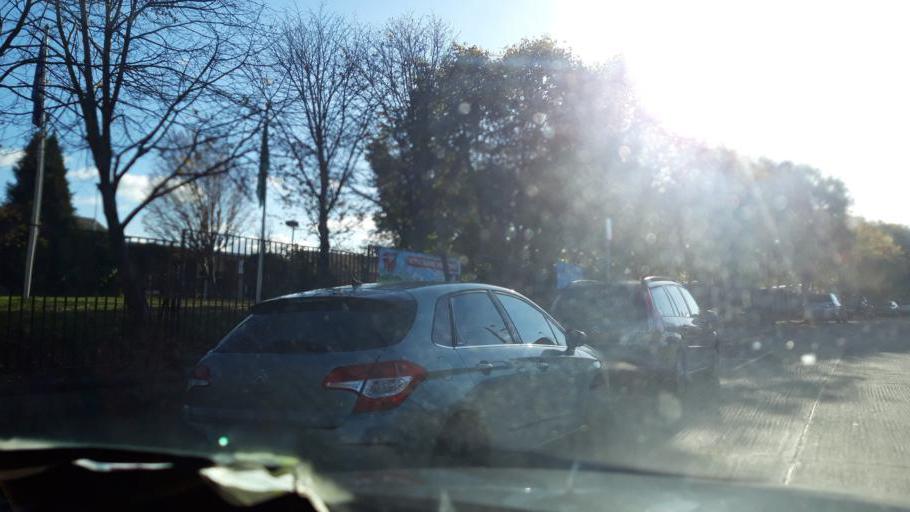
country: IE
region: Leinster
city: Raheny
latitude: 53.3789
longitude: -6.1776
